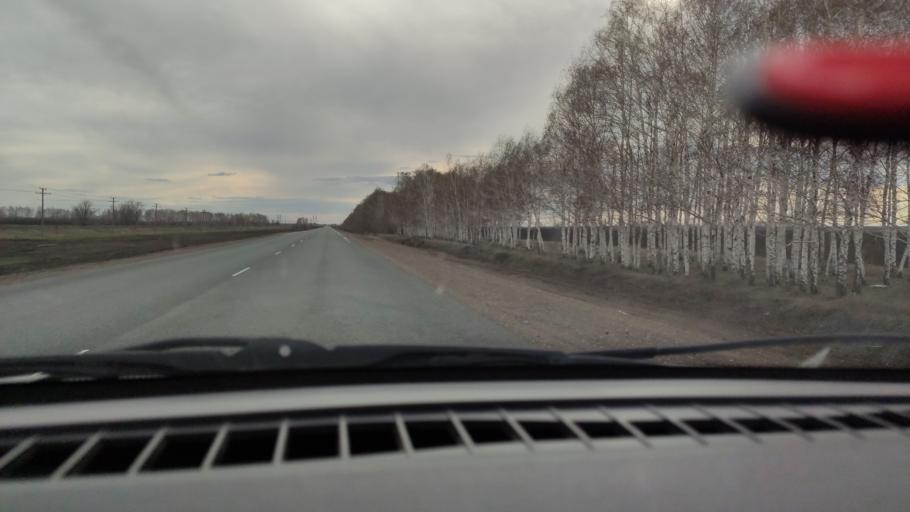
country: RU
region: Bashkortostan
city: Mayachnyy
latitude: 52.3758
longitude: 55.6344
